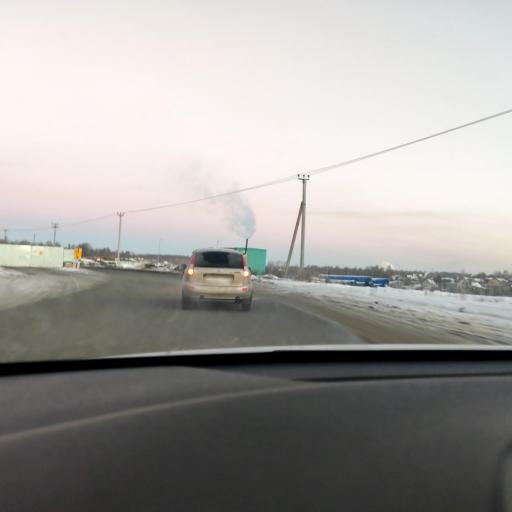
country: RU
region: Tatarstan
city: Osinovo
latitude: 55.8572
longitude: 48.9115
